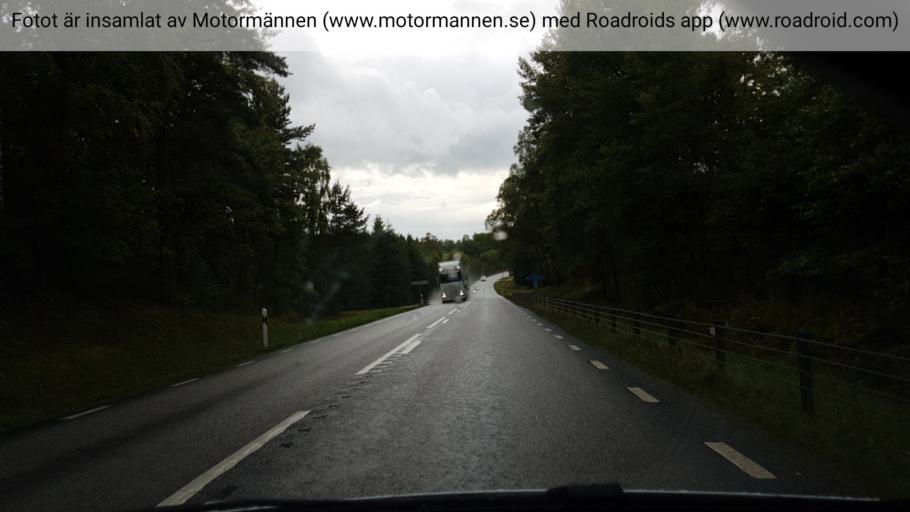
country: SE
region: Joenkoeping
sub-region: Mullsjo Kommun
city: Mullsjoe
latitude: 58.0483
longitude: 13.8120
